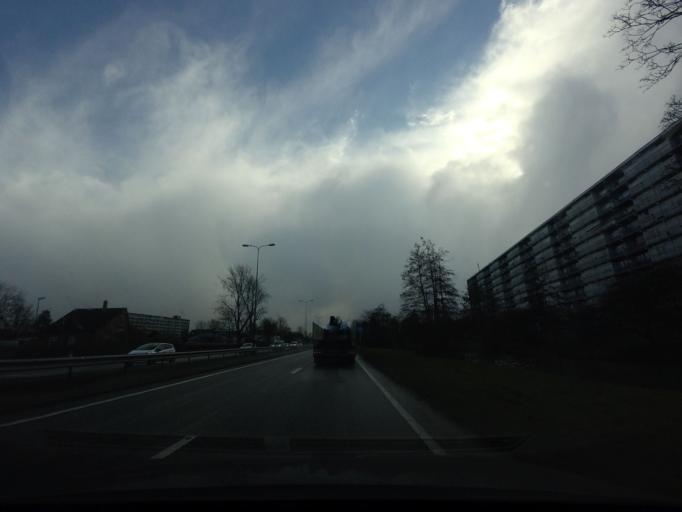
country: NL
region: Groningen
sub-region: Gemeente Groningen
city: Korrewegwijk
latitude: 53.2295
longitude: 6.5319
